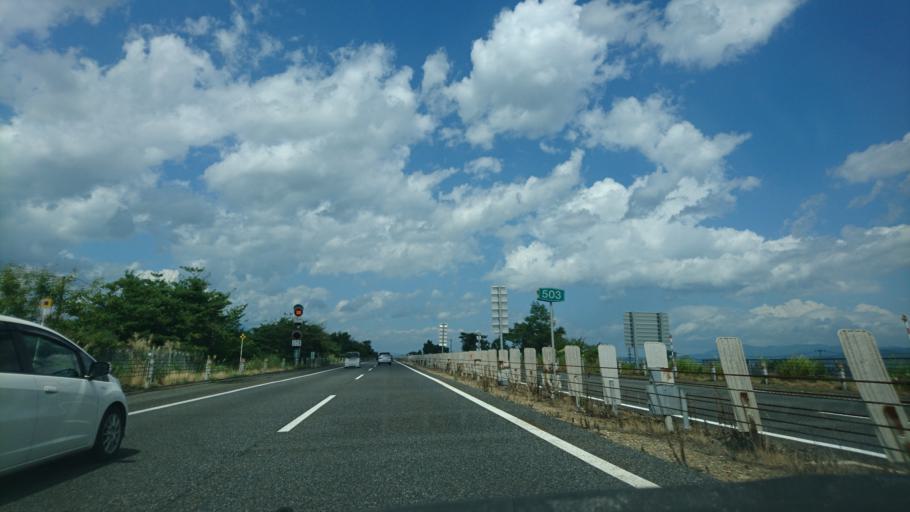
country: JP
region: Iwate
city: Morioka-shi
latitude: 39.6343
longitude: 141.1270
